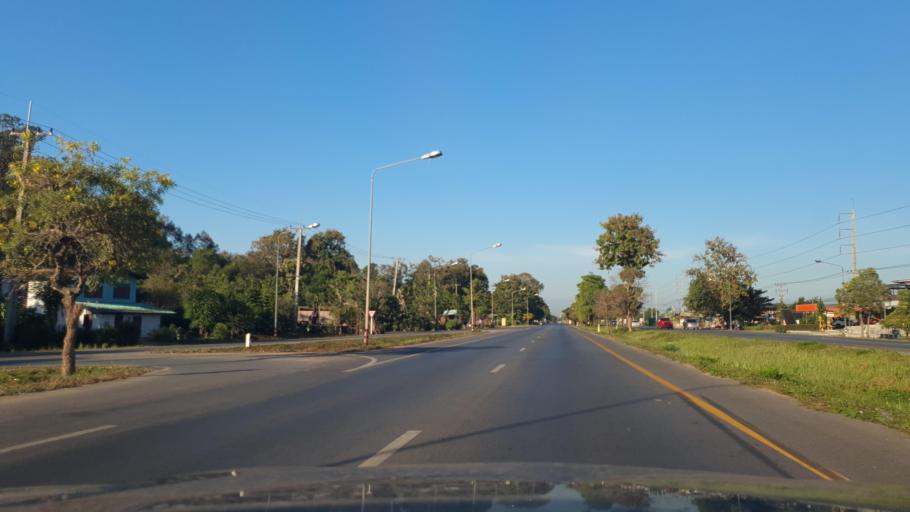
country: TH
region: Phitsanulok
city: Phitsanulok
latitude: 16.8649
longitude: 100.2423
